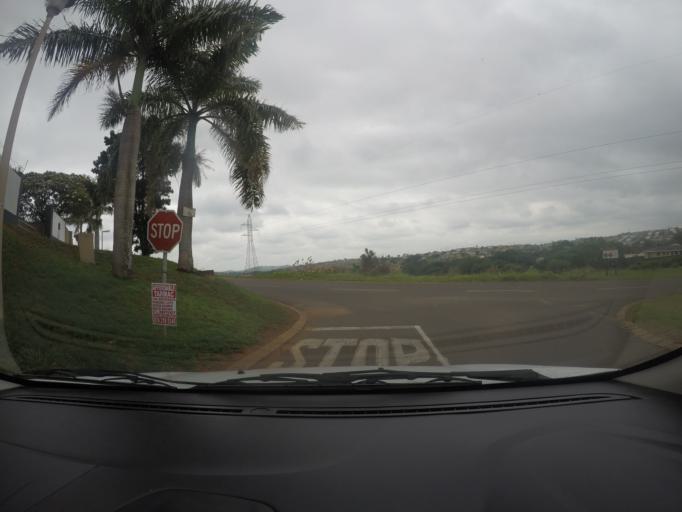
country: ZA
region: KwaZulu-Natal
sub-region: uThungulu District Municipality
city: Empangeni
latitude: -28.7616
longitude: 31.8853
